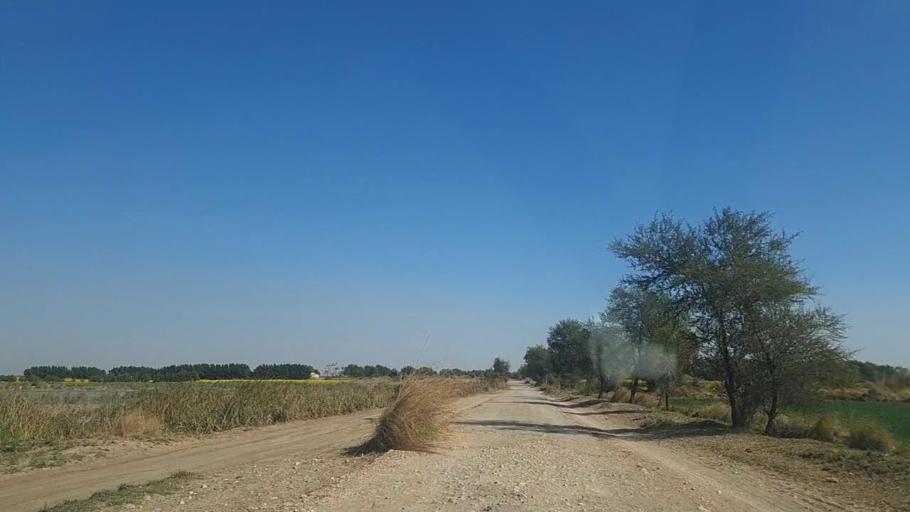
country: PK
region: Sindh
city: Sanghar
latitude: 26.2092
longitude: 68.9044
